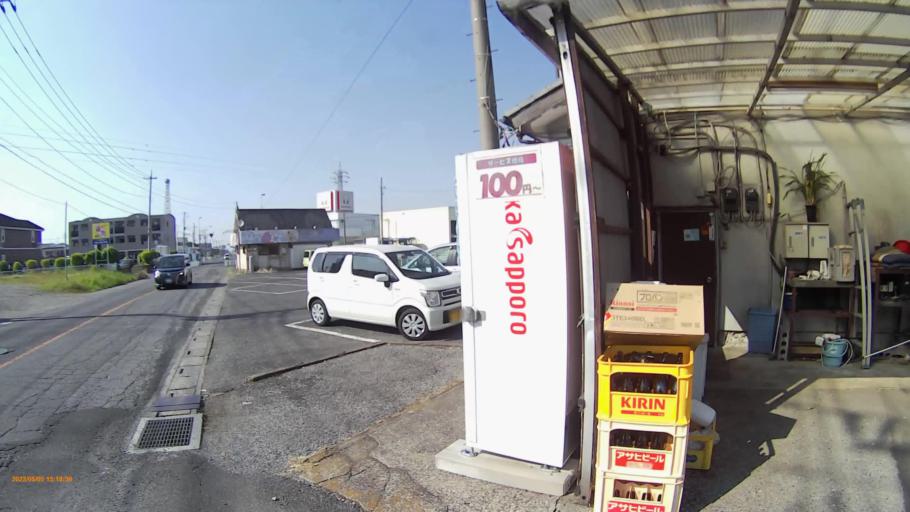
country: JP
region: Saitama
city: Sugito
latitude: 36.0345
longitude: 139.7237
